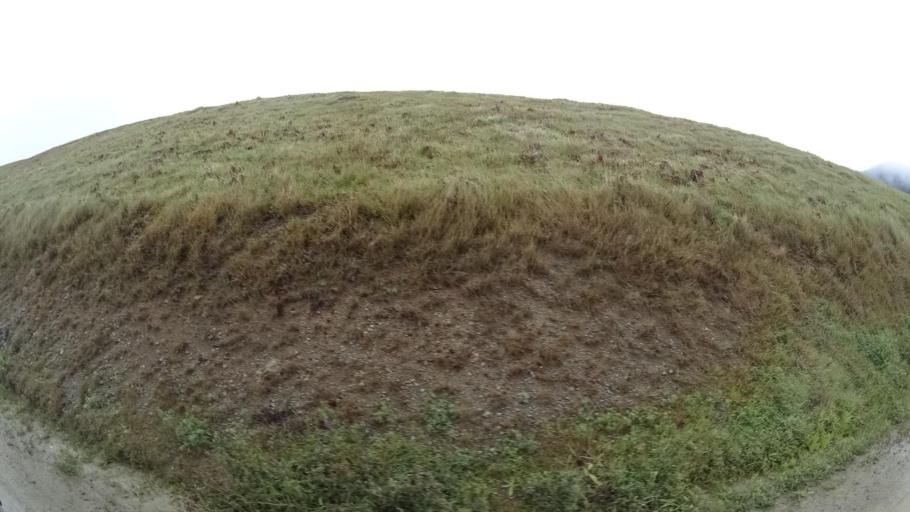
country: US
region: California
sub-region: Humboldt County
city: Westhaven-Moonstone
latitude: 41.1448
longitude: -123.8680
